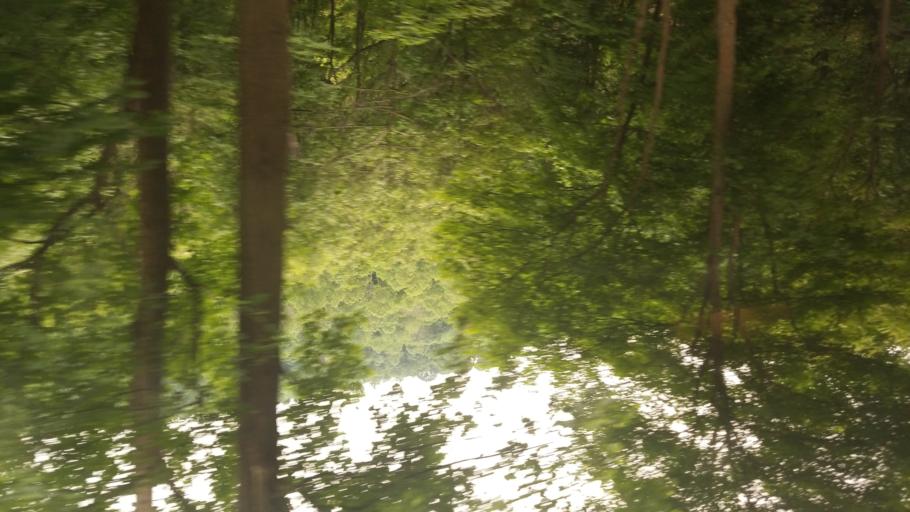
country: US
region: Pennsylvania
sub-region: Fayette County
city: South Connellsville
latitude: 39.9291
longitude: -79.4869
